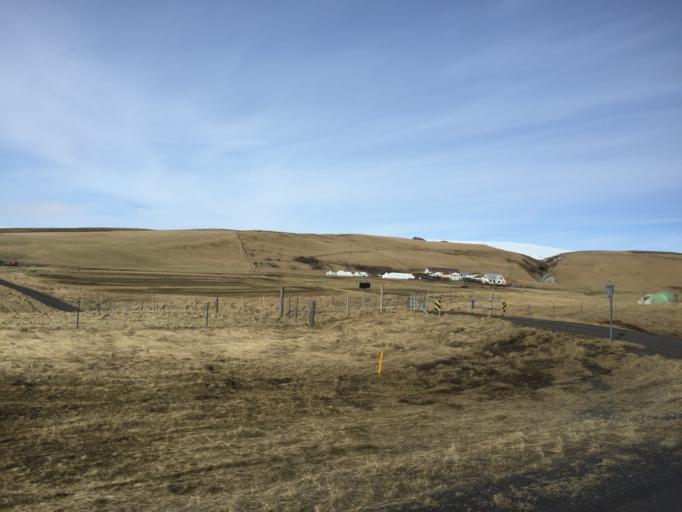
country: IS
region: South
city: Vestmannaeyjar
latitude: 63.4325
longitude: -19.1728
